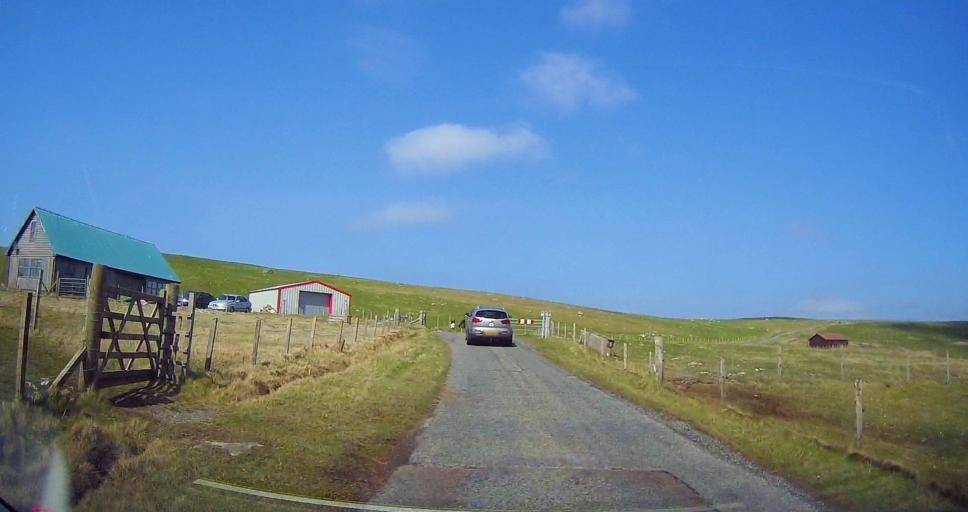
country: GB
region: Scotland
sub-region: Shetland Islands
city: Sandwick
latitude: 60.0700
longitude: -1.3400
